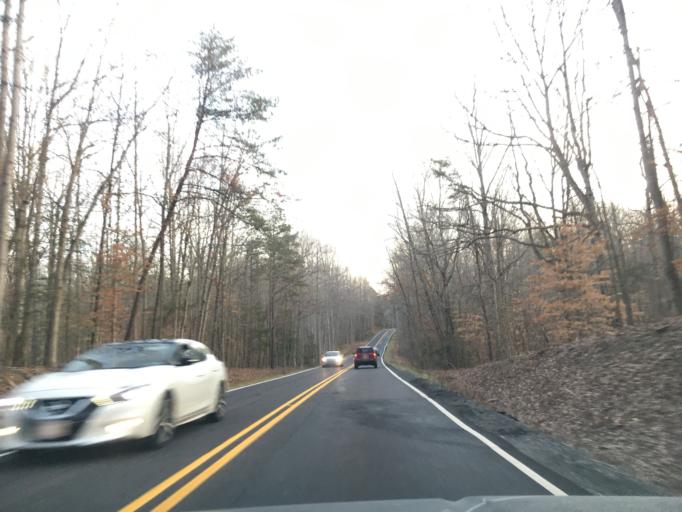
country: US
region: Virginia
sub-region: Louisa County
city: Louisa
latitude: 38.1519
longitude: -77.9271
